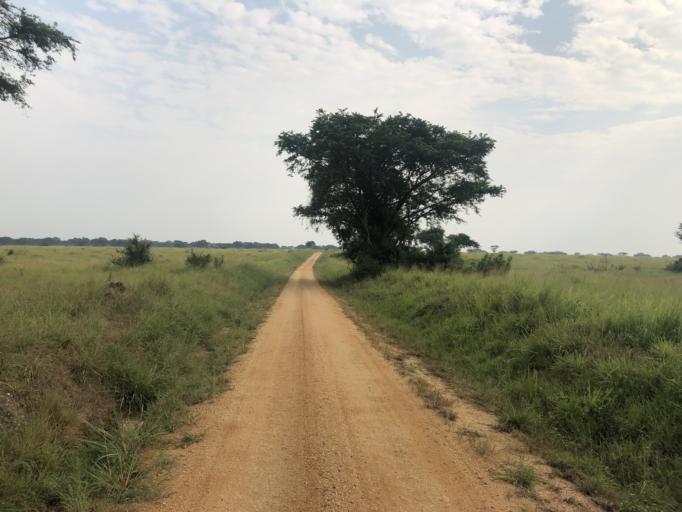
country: UG
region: Western Region
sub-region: Mitoma District
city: Mitoma
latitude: -0.5025
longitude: 29.8025
